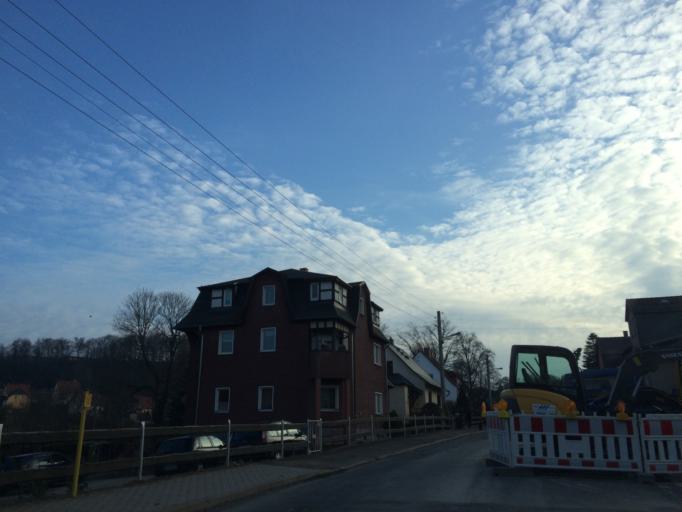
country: DE
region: Thuringia
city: Konitz
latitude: 50.6557
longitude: 11.4912
